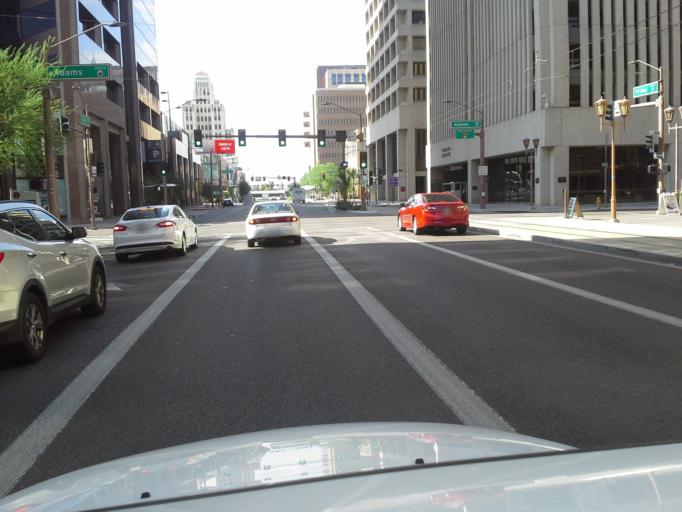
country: US
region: Arizona
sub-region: Maricopa County
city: Phoenix
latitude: 33.4496
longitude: -112.0751
